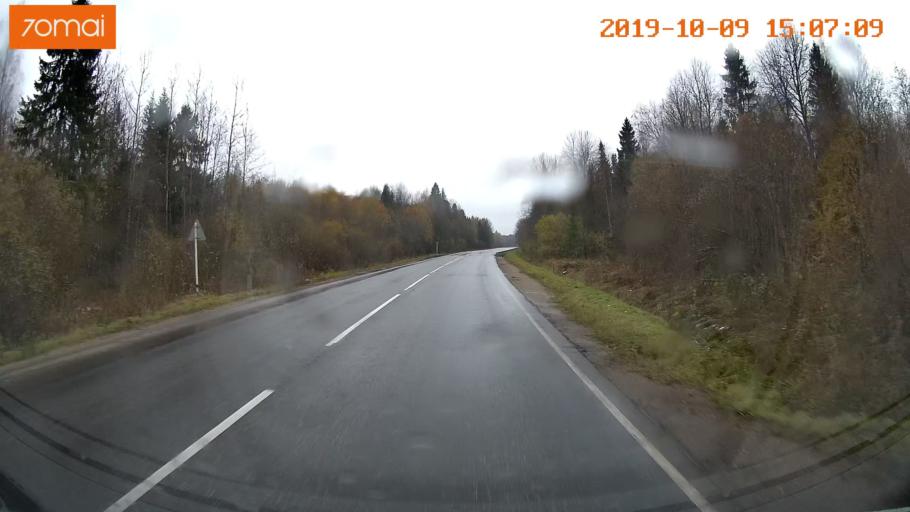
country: RU
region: Kostroma
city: Susanino
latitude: 58.2229
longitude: 41.6530
